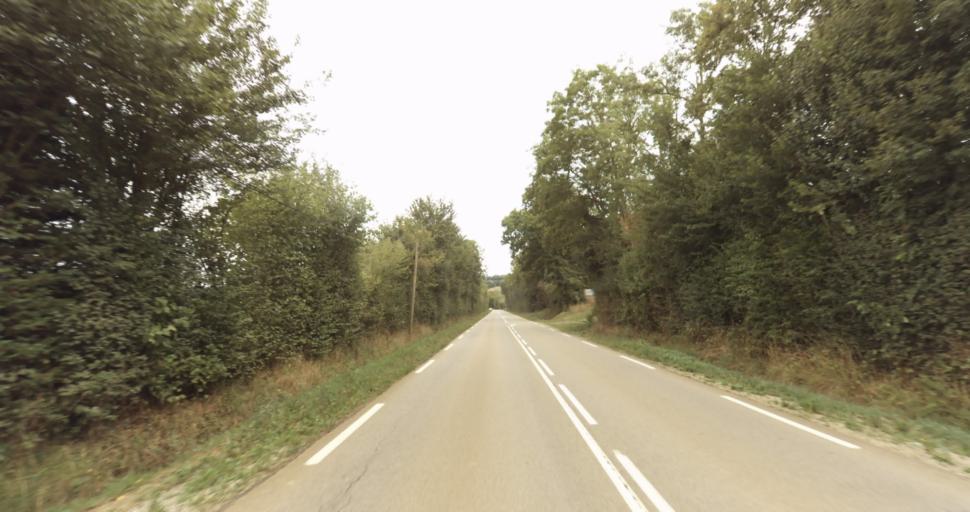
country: FR
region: Lower Normandy
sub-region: Departement de l'Orne
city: Gace
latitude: 48.7623
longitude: 0.3360
